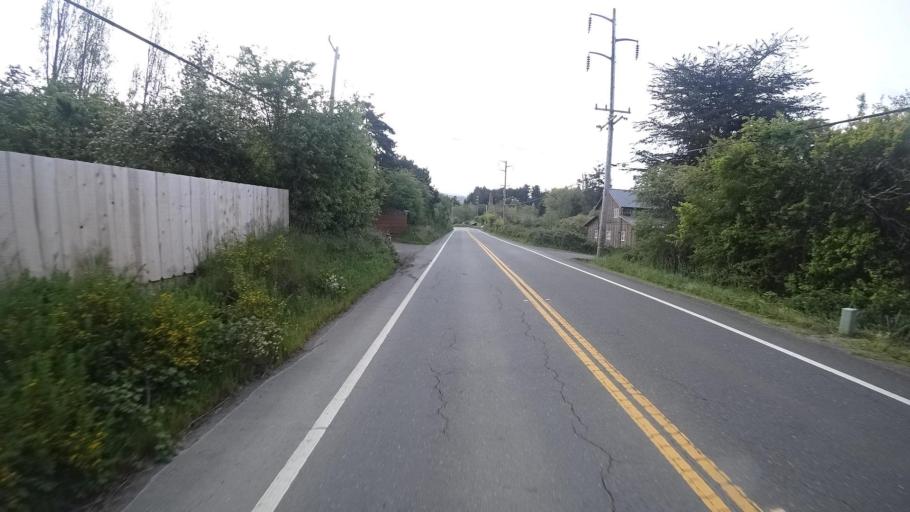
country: US
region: California
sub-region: Humboldt County
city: Myrtletown
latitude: 40.7660
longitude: -124.0674
